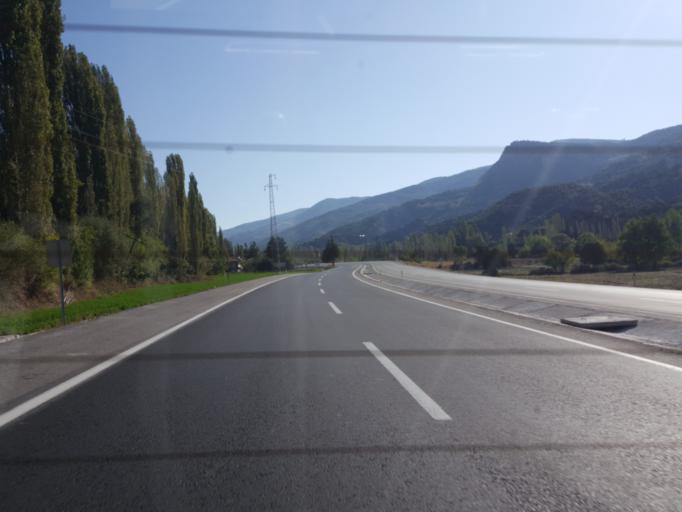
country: TR
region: Tokat
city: Turhal
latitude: 40.4748
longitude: 36.1408
